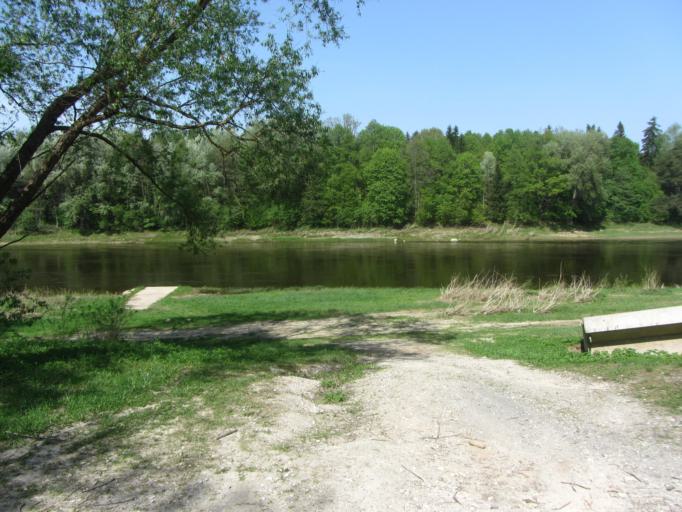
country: LT
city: Birstonas
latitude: 54.5126
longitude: 24.0875
